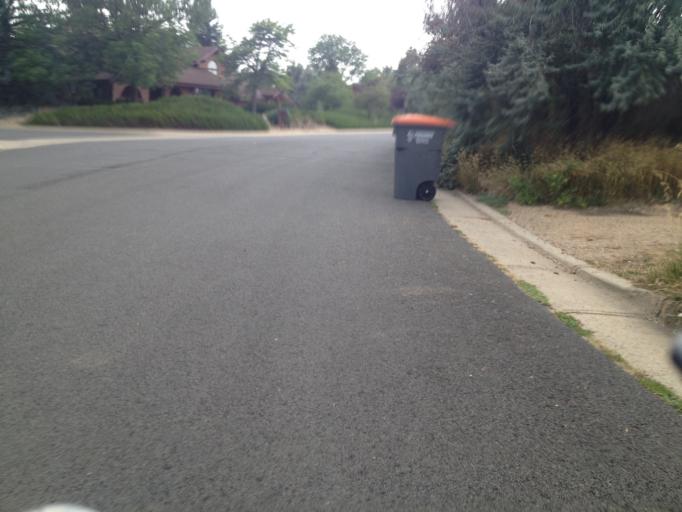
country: US
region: Colorado
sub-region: Boulder County
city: Louisville
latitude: 39.9889
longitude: -105.1630
